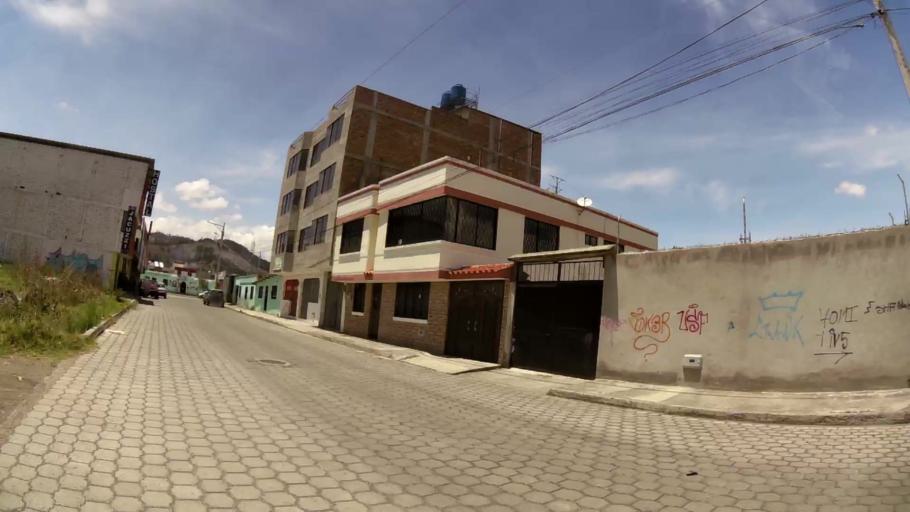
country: EC
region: Chimborazo
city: Riobamba
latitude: -1.6832
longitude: -78.6527
